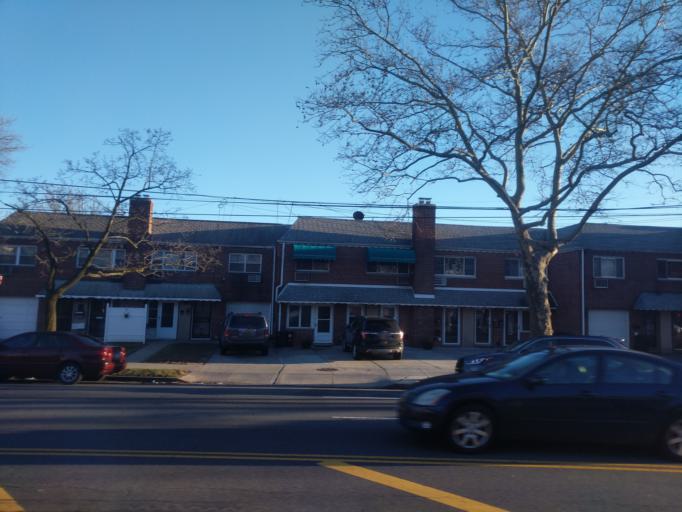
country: US
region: New York
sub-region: Nassau County
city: Bellerose Terrace
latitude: 40.7259
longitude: -73.7521
